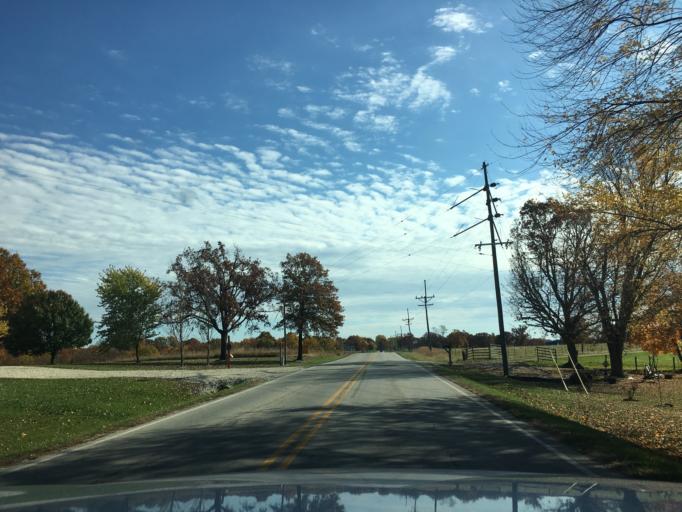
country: US
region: Missouri
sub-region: Maries County
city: Belle
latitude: 38.3008
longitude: -91.7252
